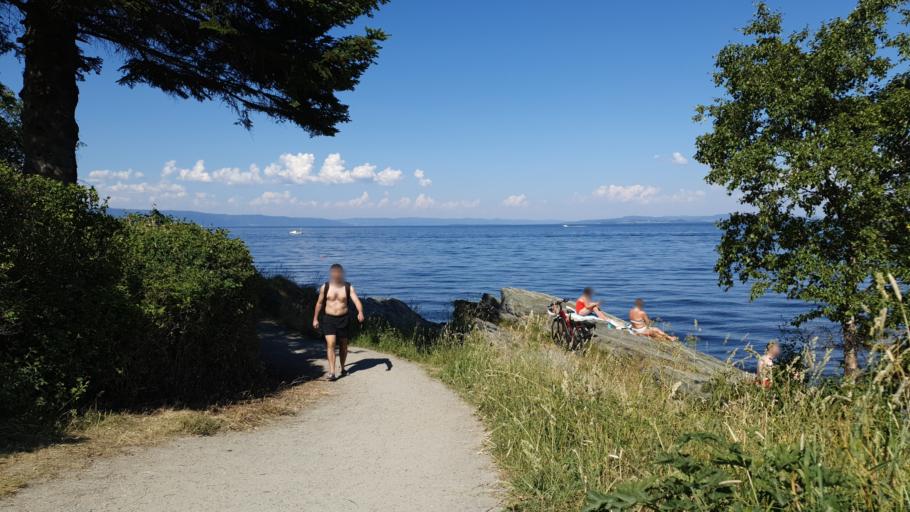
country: NO
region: Sor-Trondelag
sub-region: Trondheim
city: Trondheim
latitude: 63.4534
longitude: 10.4619
